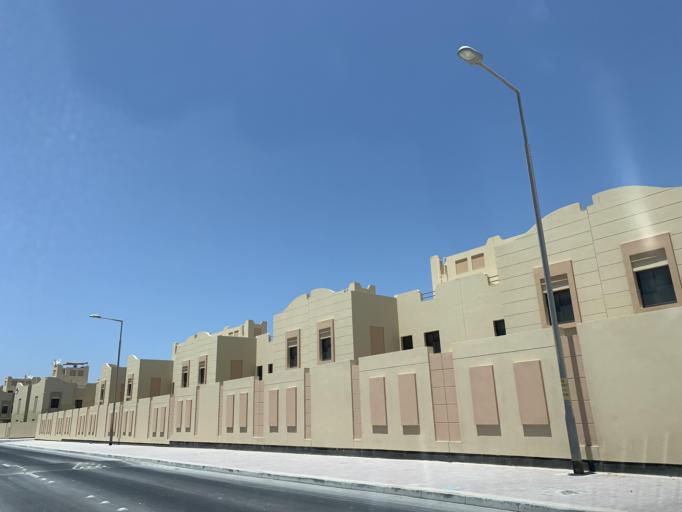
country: BH
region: Manama
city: Jidd Hafs
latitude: 26.2317
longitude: 50.4923
